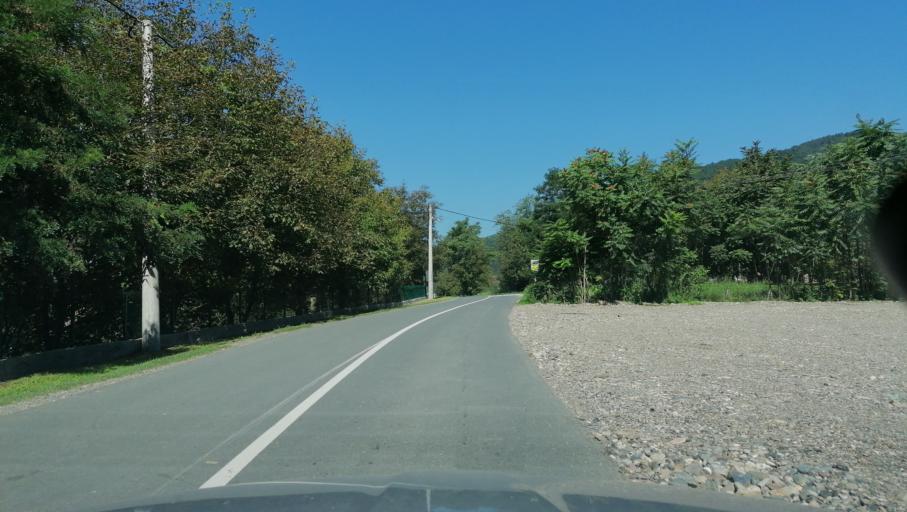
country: RS
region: Central Serbia
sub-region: Raski Okrug
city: Vrnjacka Banja
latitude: 43.6531
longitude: 20.9368
